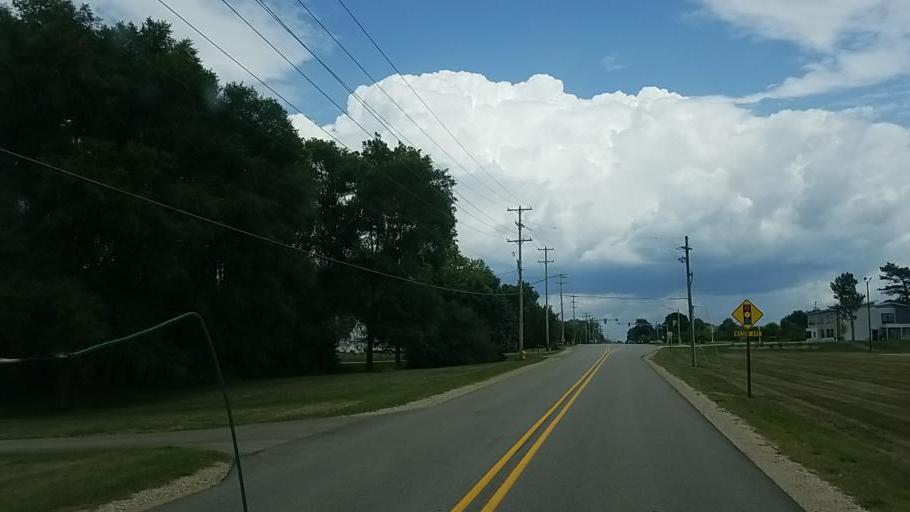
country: US
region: Michigan
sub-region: Kent County
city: Walker
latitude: 43.0160
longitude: -85.7807
